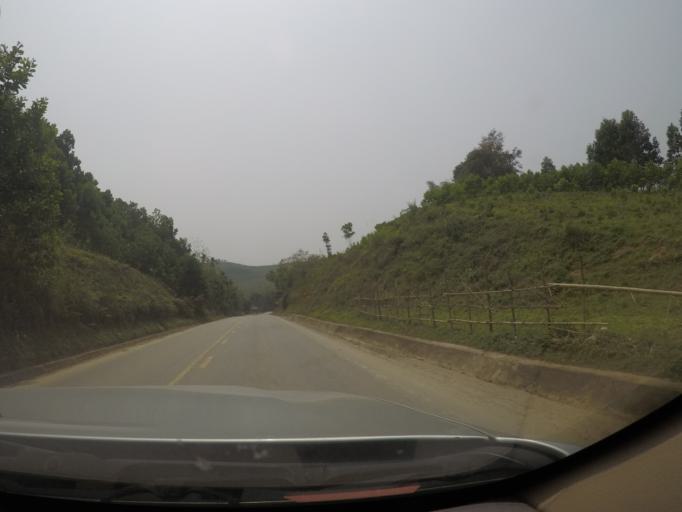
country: VN
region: Thanh Hoa
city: Thi Tran Thuong Xuan
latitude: 19.8373
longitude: 105.3986
